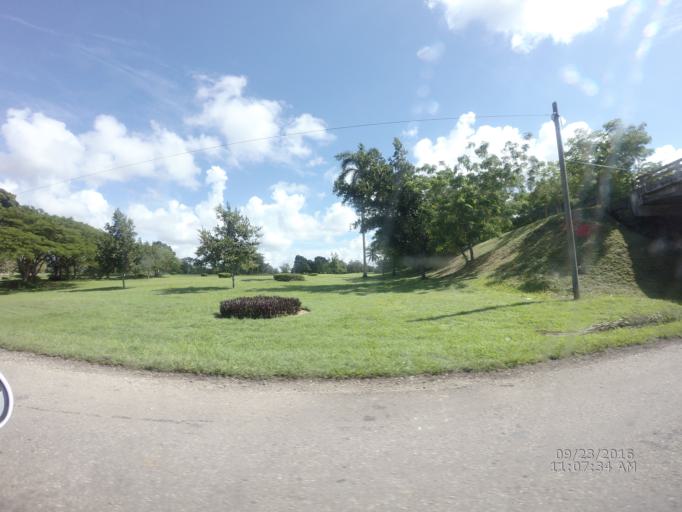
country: CU
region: Mayabeque
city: Jamaica
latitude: 23.0161
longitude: -82.2294
